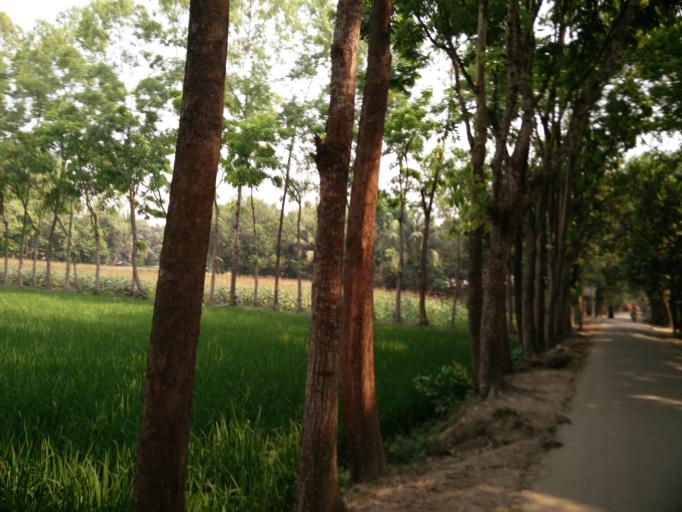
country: BD
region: Dhaka
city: Muktagacha
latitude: 24.9137
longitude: 90.2162
